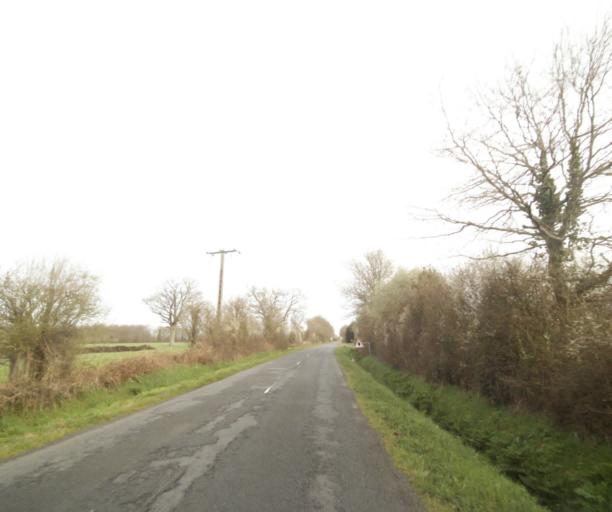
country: FR
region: Pays de la Loire
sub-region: Departement de la Loire-Atlantique
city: Bouvron
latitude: 47.4001
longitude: -1.8844
